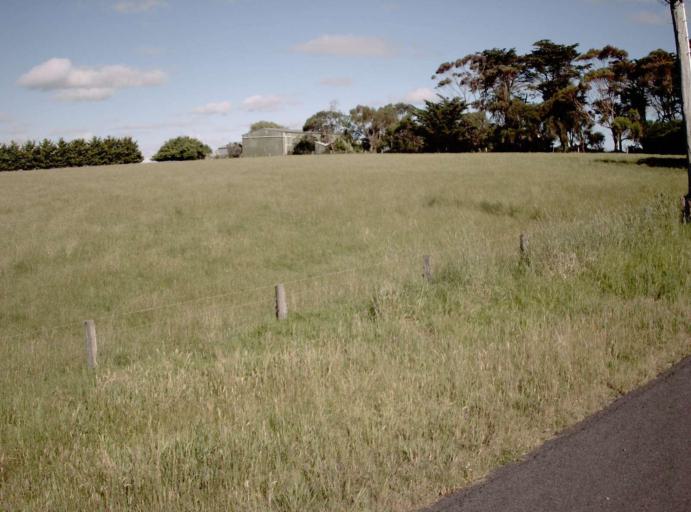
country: AU
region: Victoria
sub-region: Bass Coast
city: North Wonthaggi
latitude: -38.5335
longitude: 145.4533
